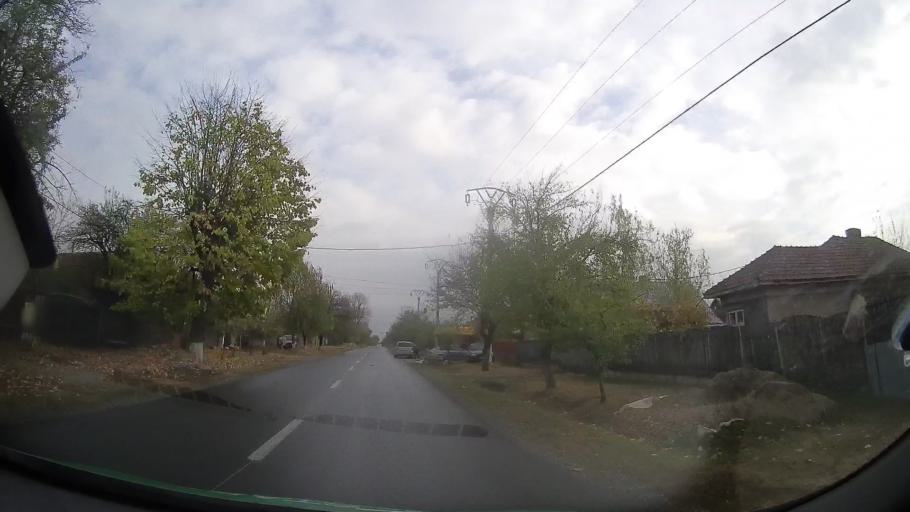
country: RO
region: Ialomita
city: Brazii
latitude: 44.7605
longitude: 26.3627
